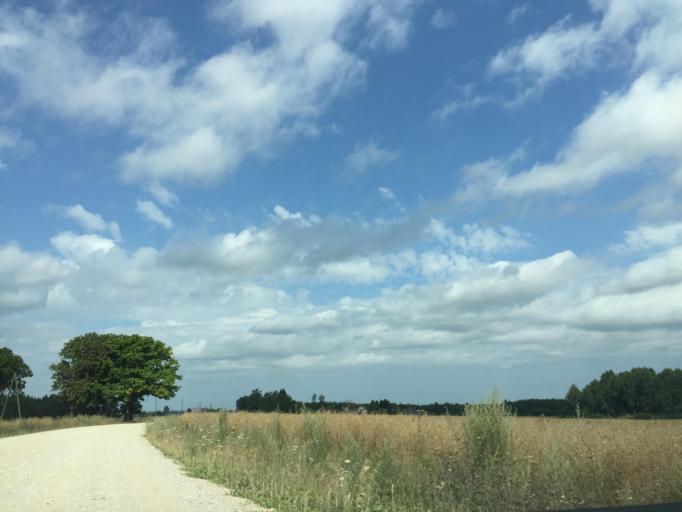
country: LV
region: Kandava
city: Kandava
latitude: 56.9852
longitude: 22.9072
